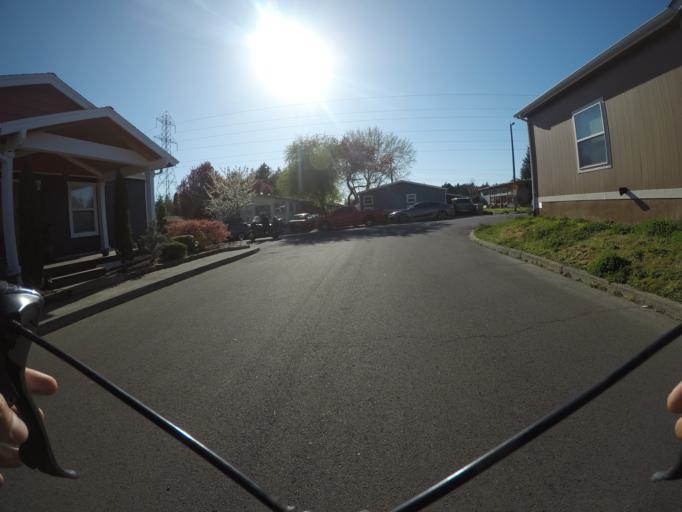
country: US
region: Oregon
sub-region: Washington County
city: King City
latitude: 45.4017
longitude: -122.8171
